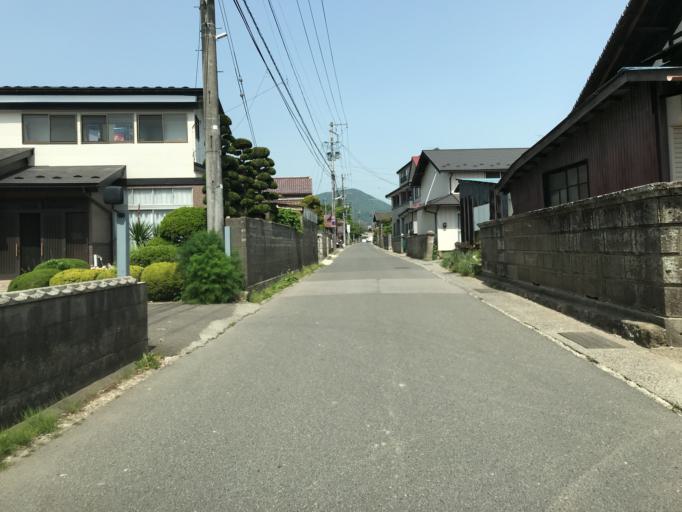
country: JP
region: Fukushima
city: Fukushima-shi
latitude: 37.8283
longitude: 140.4626
